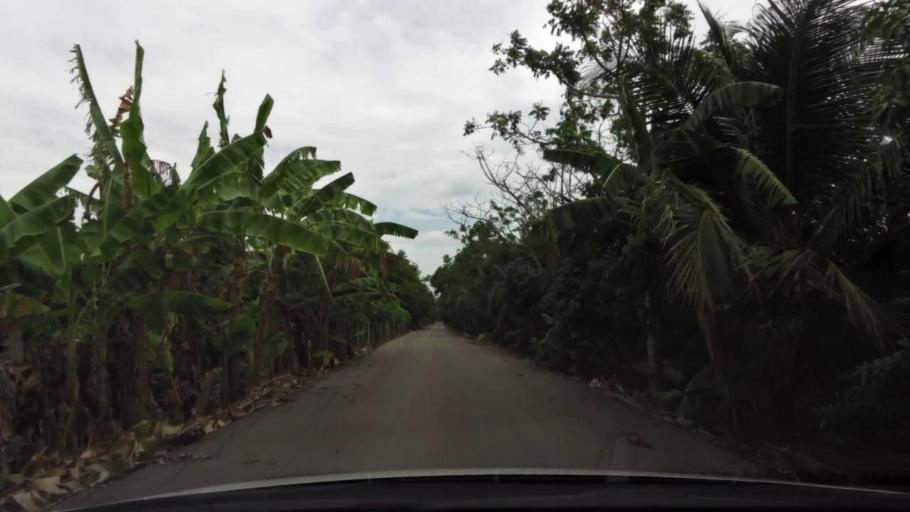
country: TH
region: Ratchaburi
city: Damnoen Saduak
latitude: 13.5522
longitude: 100.0032
